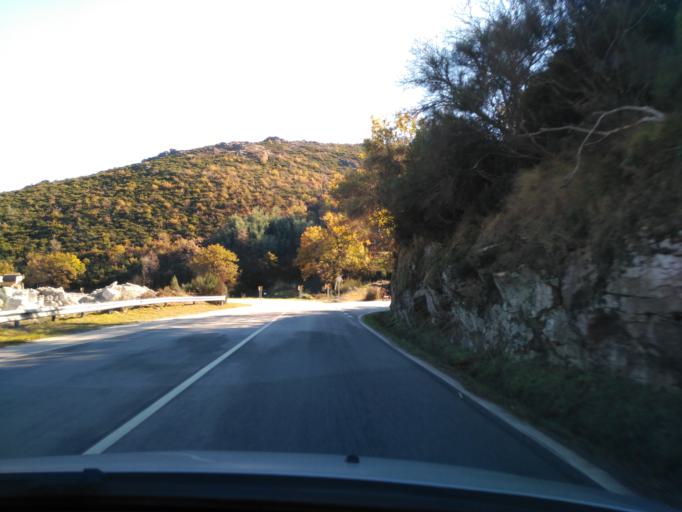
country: PT
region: Braga
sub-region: Vieira do Minho
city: Vieira do Minho
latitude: 41.6810
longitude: -7.9945
